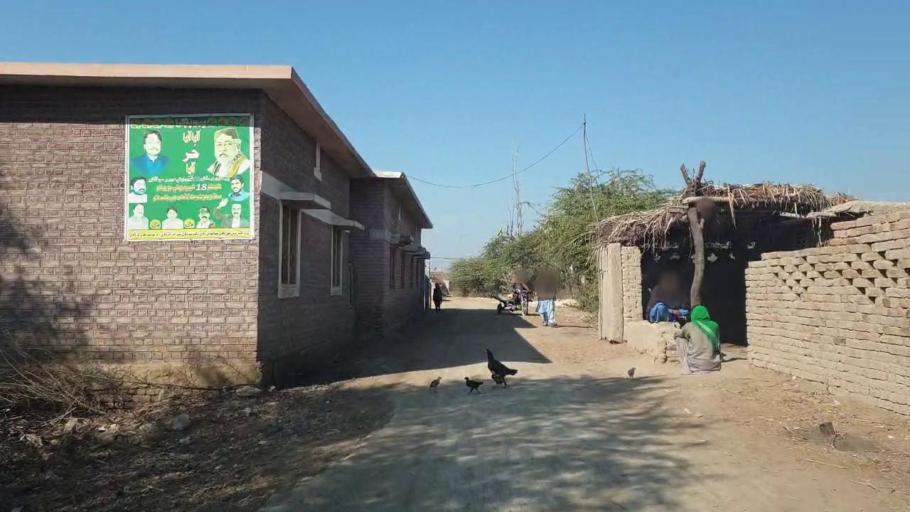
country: PK
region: Sindh
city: Shahpur Chakar
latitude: 26.0781
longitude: 68.6472
